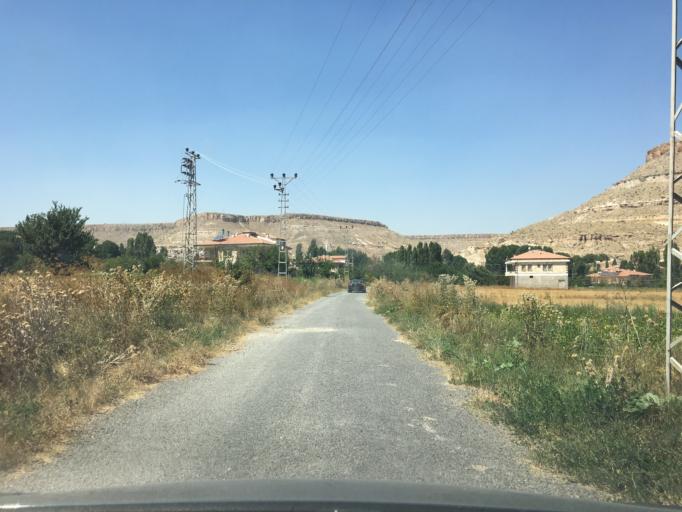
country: TR
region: Nevsehir
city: Urgub
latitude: 38.4678
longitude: 34.9632
